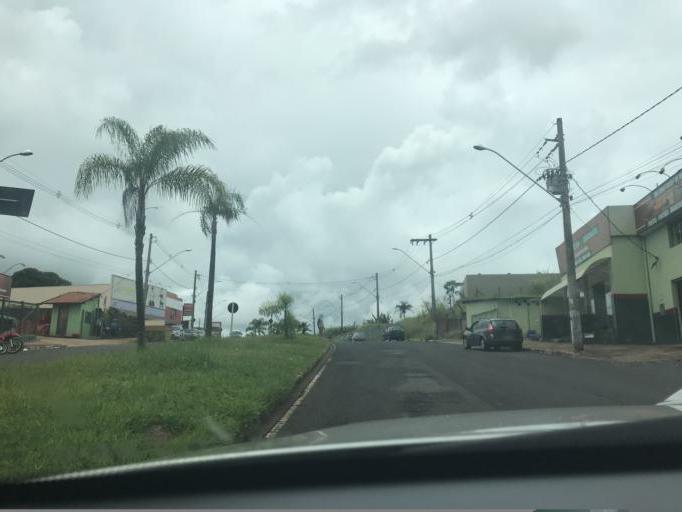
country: BR
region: Minas Gerais
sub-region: Araxa
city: Araxa
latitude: -19.5804
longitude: -46.9380
